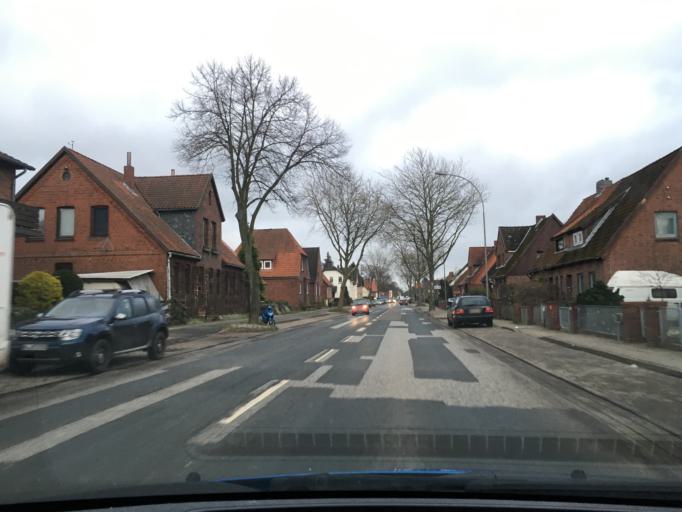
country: DE
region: Lower Saxony
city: Winsen
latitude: 53.3657
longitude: 10.1914
